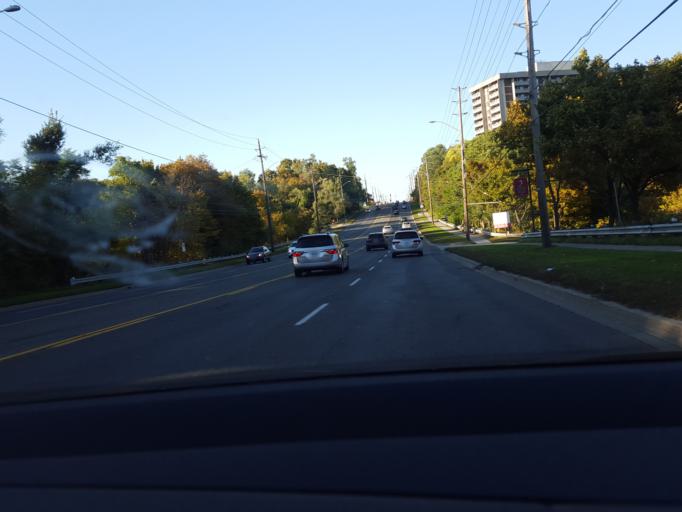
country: CA
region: Ontario
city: North York
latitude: 43.8185
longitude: -79.4249
